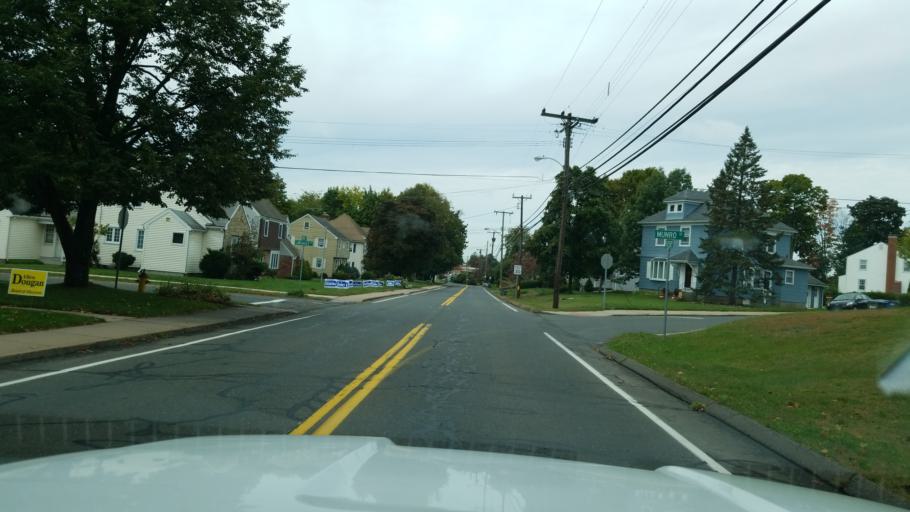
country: US
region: Connecticut
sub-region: Hartford County
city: Manchester
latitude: 41.7766
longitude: -72.5058
